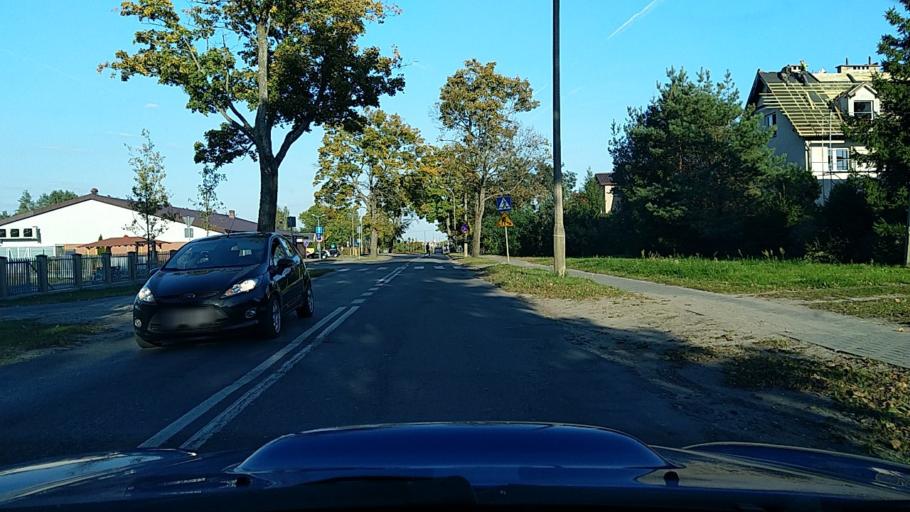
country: PL
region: Warmian-Masurian Voivodeship
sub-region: Olsztyn
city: Kortowo
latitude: 53.7683
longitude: 20.4289
